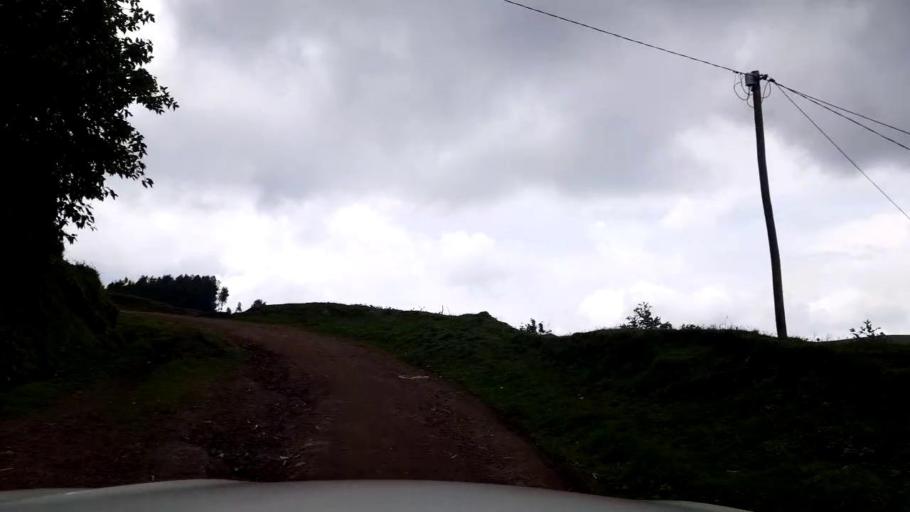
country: RW
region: Western Province
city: Gisenyi
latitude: -1.6759
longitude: 29.4125
